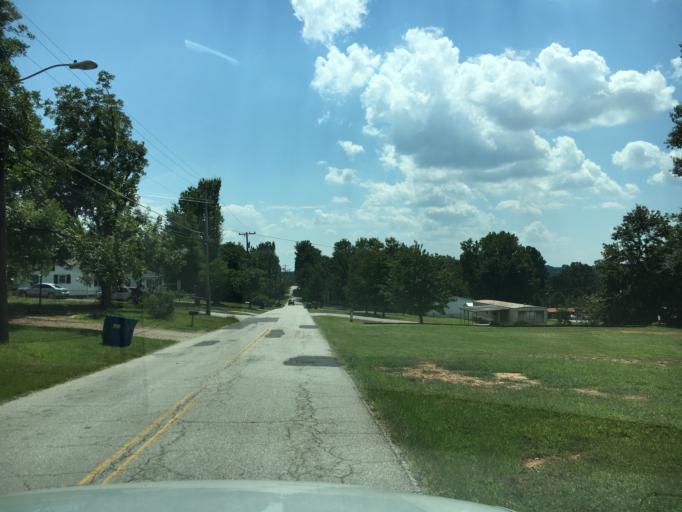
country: US
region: South Carolina
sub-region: Spartanburg County
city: Duncan
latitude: 34.9317
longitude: -82.1355
